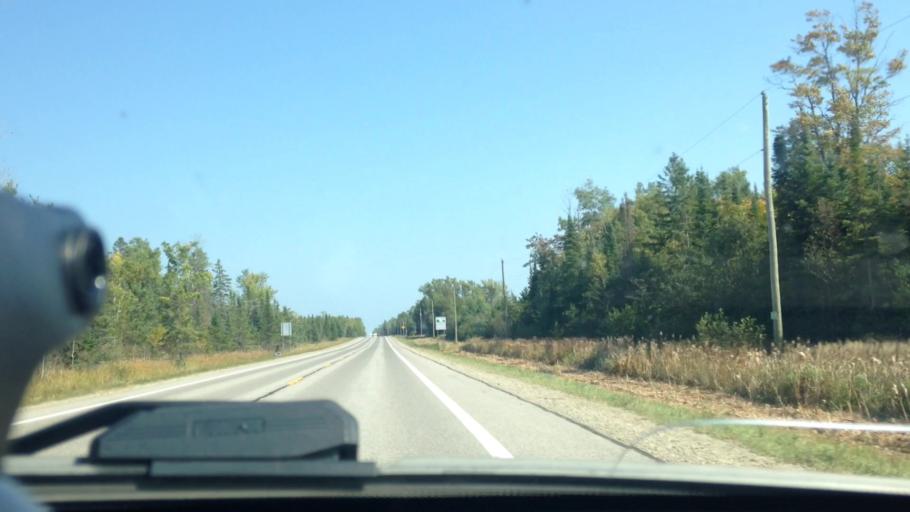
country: US
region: Michigan
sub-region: Luce County
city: Newberry
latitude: 46.3034
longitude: -85.3807
